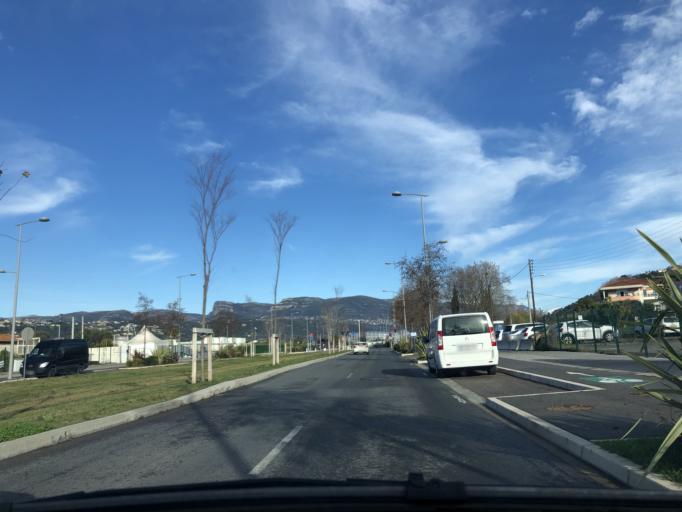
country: FR
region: Provence-Alpes-Cote d'Azur
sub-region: Departement des Alpes-Maritimes
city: Saint-Laurent-du-Var
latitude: 43.6915
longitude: 7.2001
